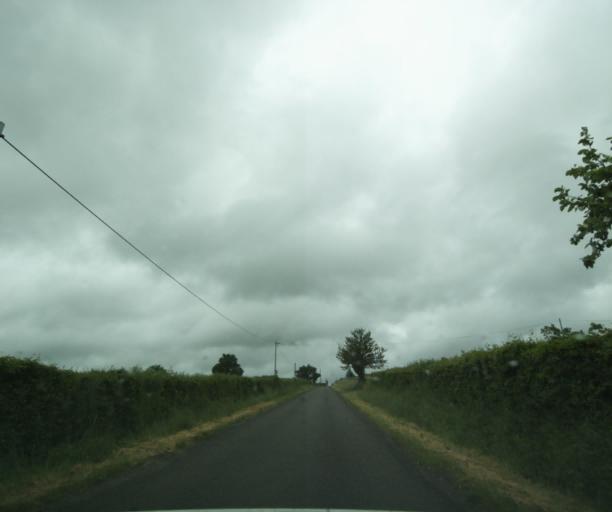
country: FR
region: Bourgogne
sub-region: Departement de Saone-et-Loire
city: Charolles
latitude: 46.4579
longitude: 4.4332
